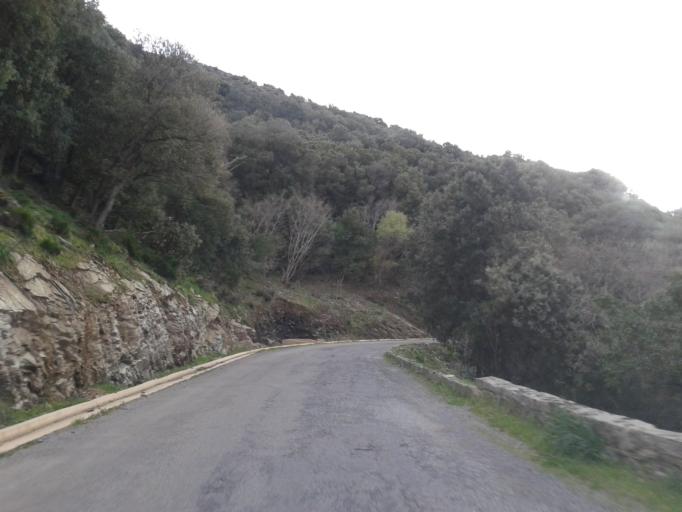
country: FR
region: Corsica
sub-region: Departement de la Haute-Corse
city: Brando
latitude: 42.9037
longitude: 9.3361
